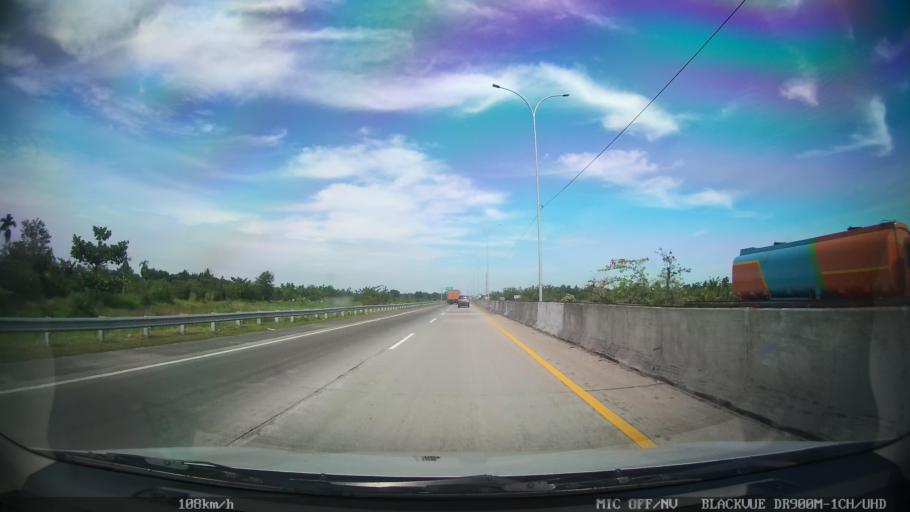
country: ID
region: North Sumatra
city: Binjai
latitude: 3.6441
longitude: 98.5591
